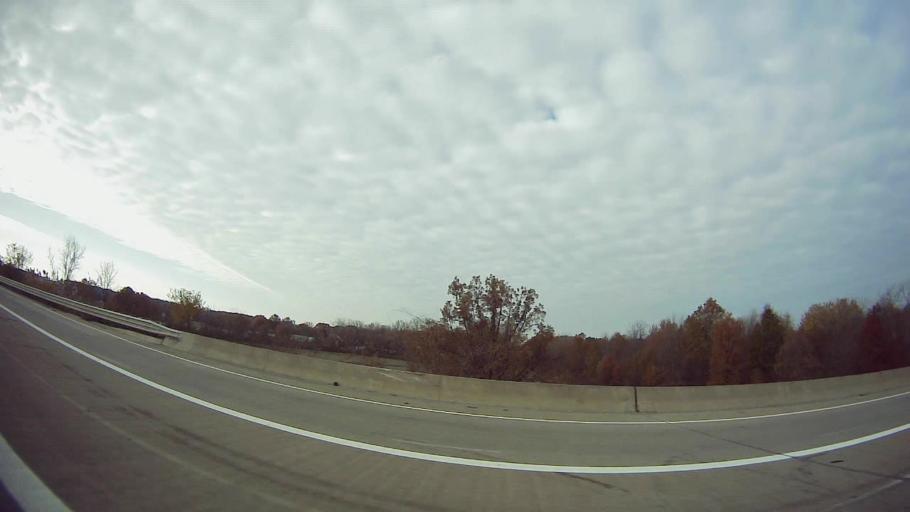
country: US
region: Michigan
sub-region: Monroe County
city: Carleton
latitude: 42.0693
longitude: -83.3652
